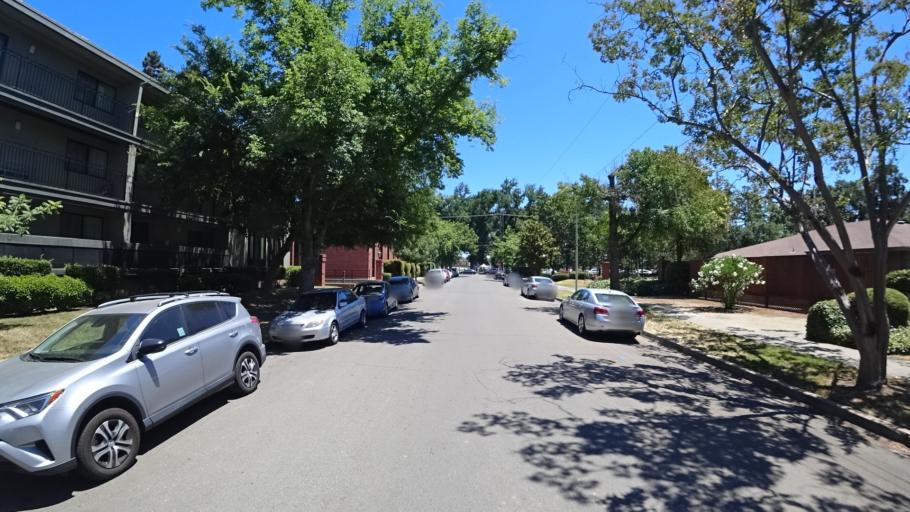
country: US
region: California
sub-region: Sacramento County
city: Sacramento
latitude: 38.5482
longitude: -121.4724
